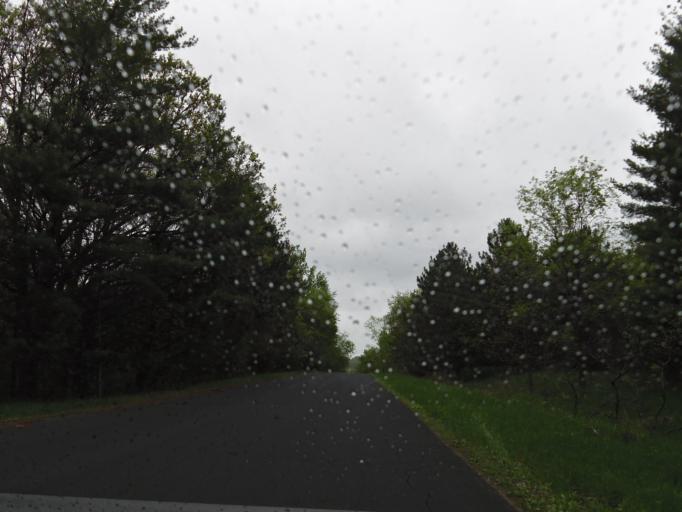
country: US
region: Minnesota
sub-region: Washington County
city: Lake Elmo
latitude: 44.9891
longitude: -92.8354
